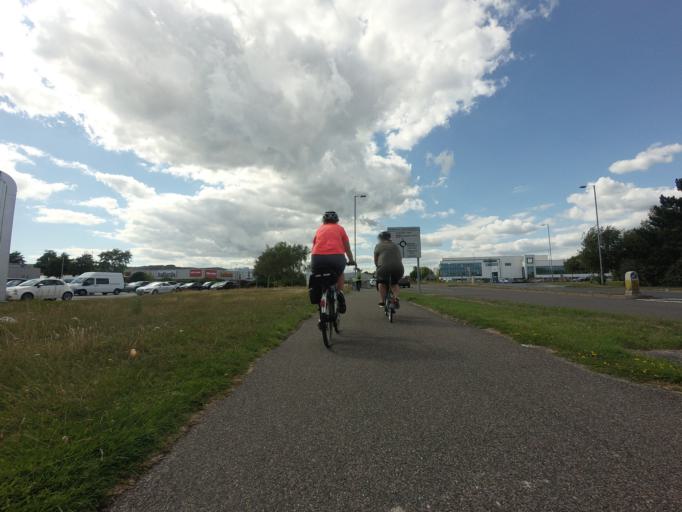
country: GB
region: England
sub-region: East Sussex
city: Eastbourne
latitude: 50.7951
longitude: 0.2865
